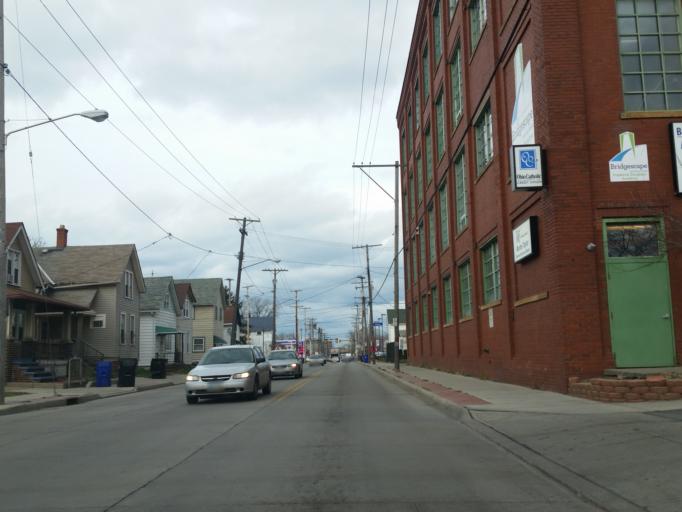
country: US
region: Ohio
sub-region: Cuyahoga County
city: Cleveland
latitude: 41.4679
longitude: -81.7074
